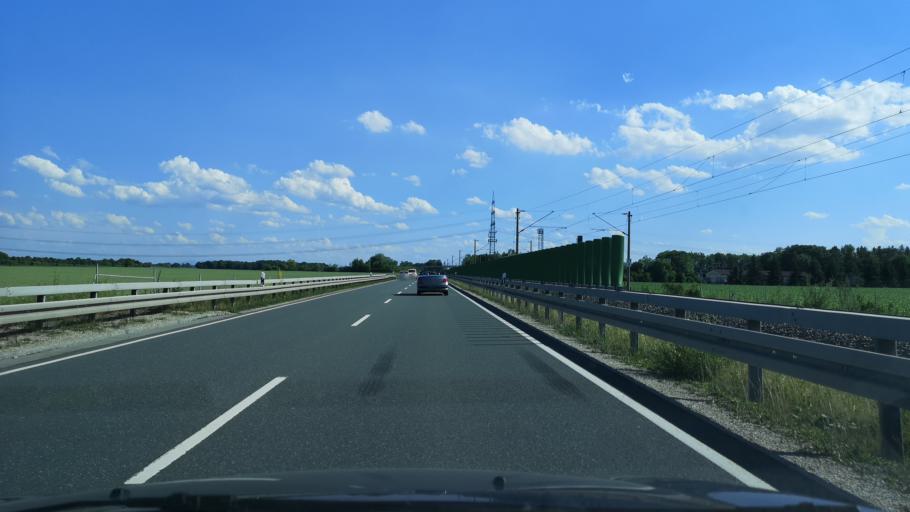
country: DE
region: Bavaria
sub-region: Upper Bavaria
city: Ismaning
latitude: 48.2824
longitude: 11.7104
